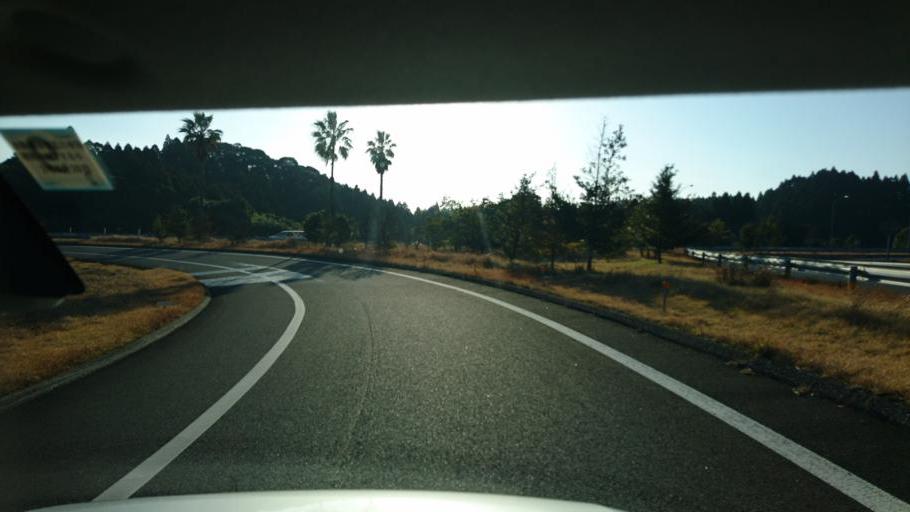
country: JP
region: Miyazaki
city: Miyazaki-shi
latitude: 31.8677
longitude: 131.3578
